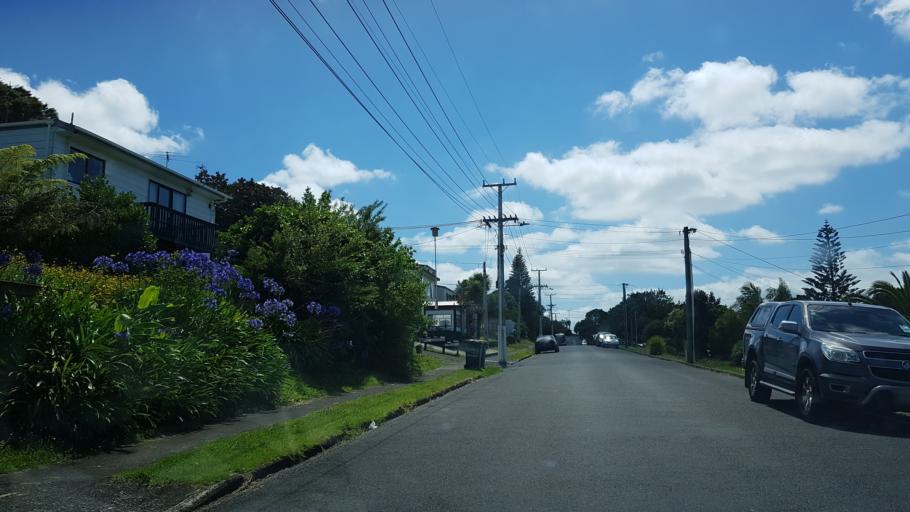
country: NZ
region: Auckland
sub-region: Auckland
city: North Shore
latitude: -36.7918
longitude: 174.7195
